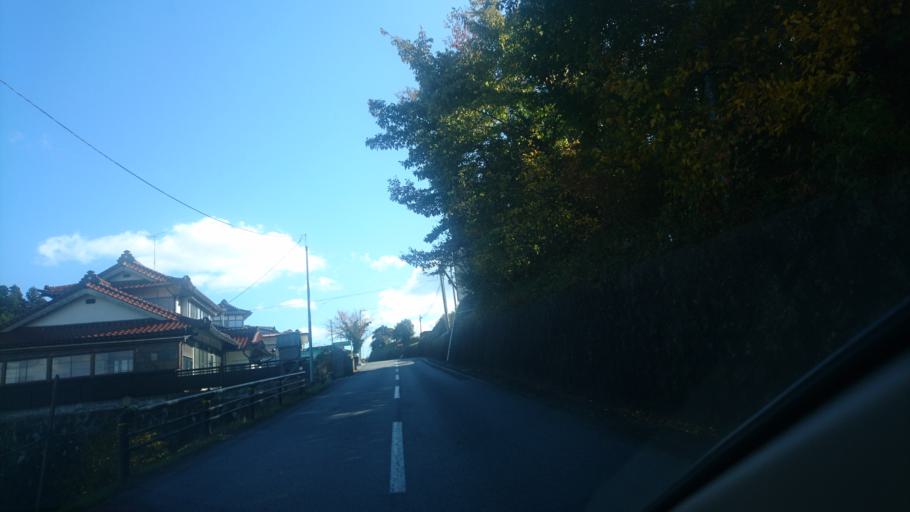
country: JP
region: Iwate
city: Ofunato
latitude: 38.9915
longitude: 141.7302
